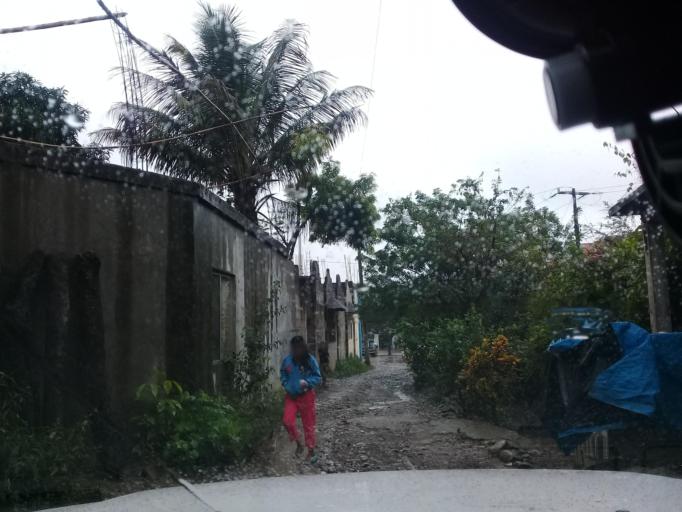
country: MX
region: Veracruz
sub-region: Chalma
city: San Pedro Coyutla
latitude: 21.1838
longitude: -98.4347
